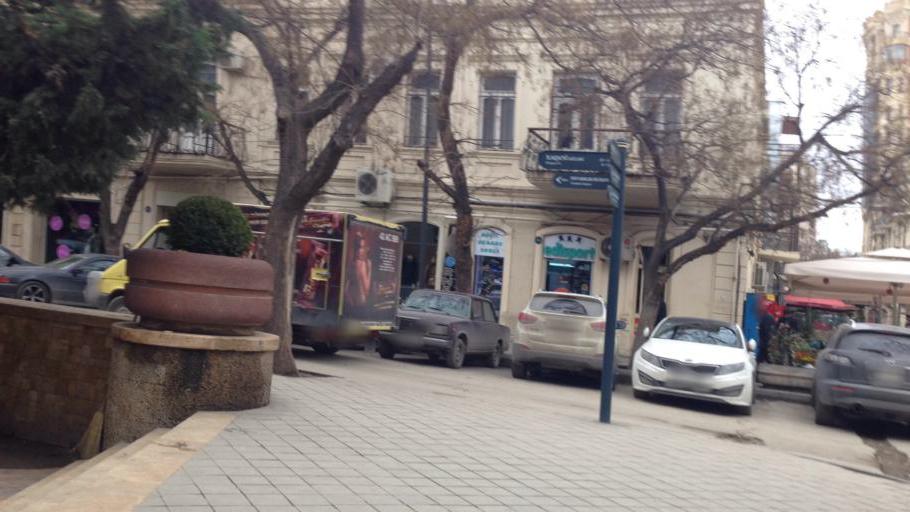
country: AZ
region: Baki
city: Badamdar
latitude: 40.3719
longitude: 49.8407
